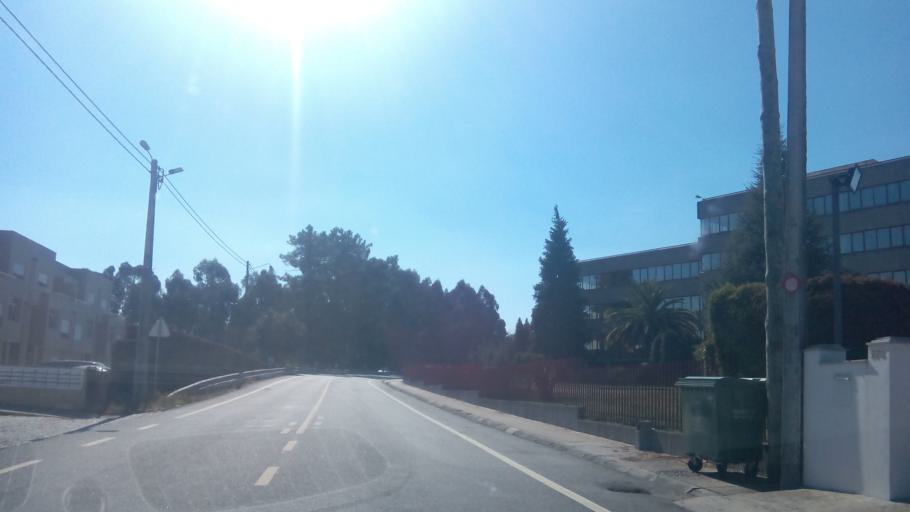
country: PT
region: Porto
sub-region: Lousada
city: Meinedo
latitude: 41.2545
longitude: -8.2138
